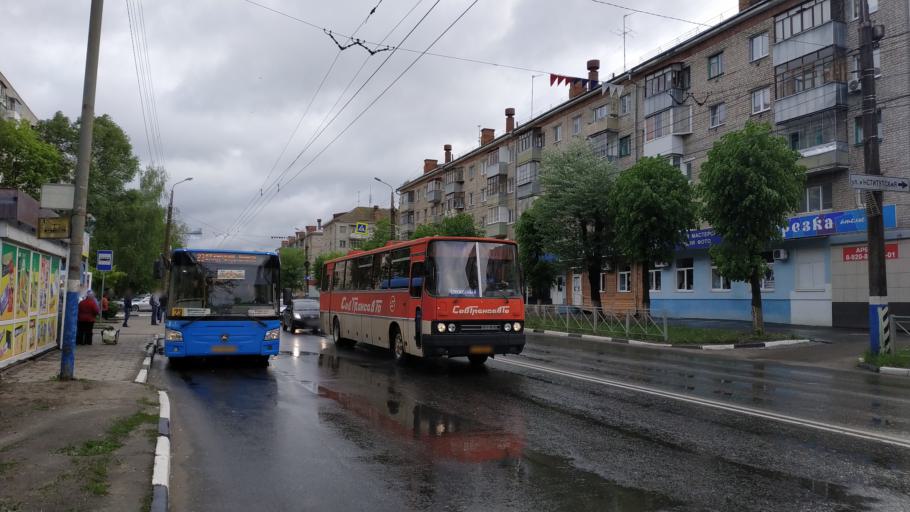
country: RU
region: Brjansk
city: Putevka
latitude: 53.3048
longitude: 34.3013
